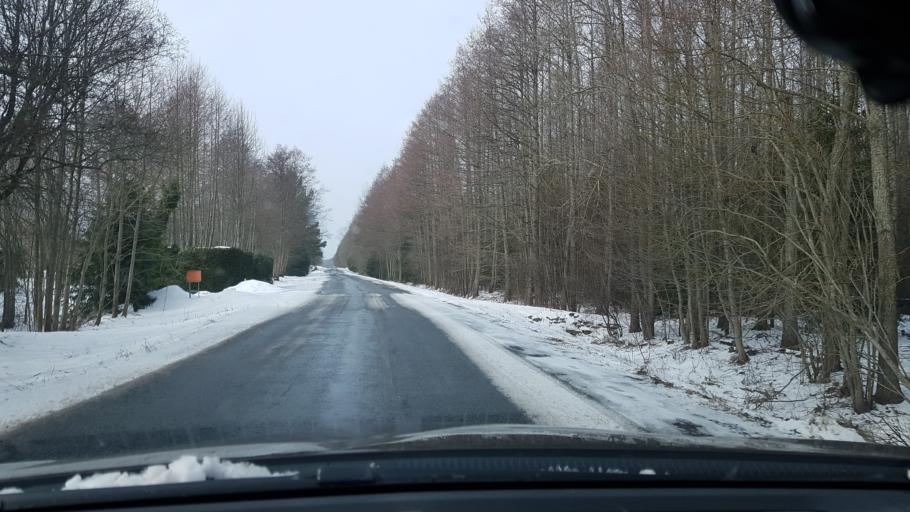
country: EE
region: Harju
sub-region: Kuusalu vald
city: Kuusalu
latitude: 59.5795
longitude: 25.5248
